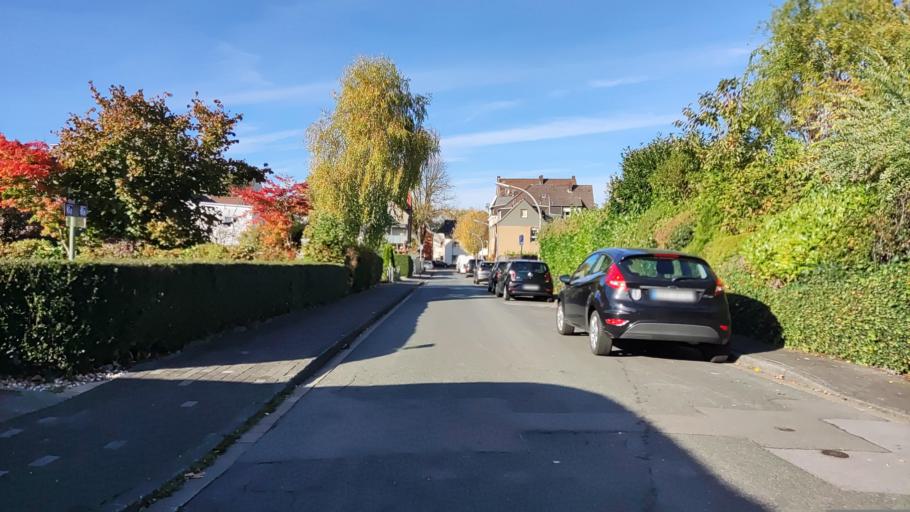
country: DE
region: North Rhine-Westphalia
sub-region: Regierungsbezirk Arnsberg
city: Herne
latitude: 51.5369
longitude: 7.2519
